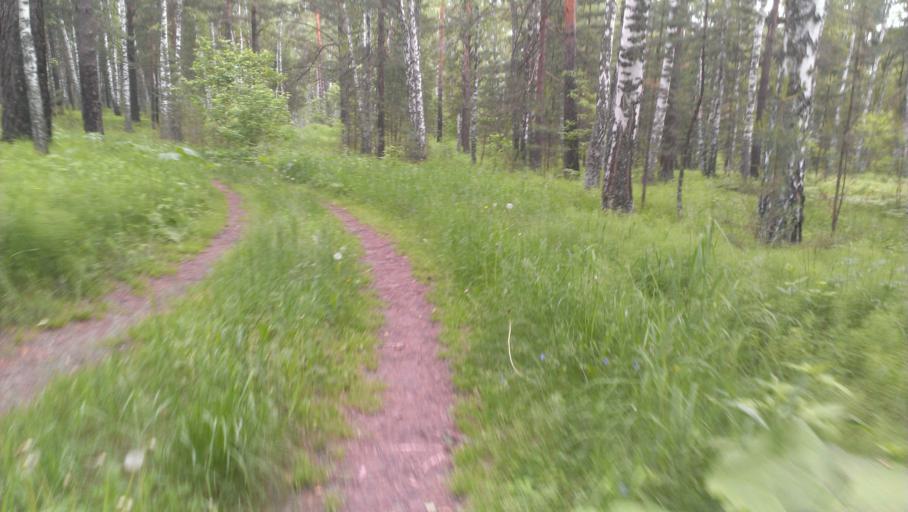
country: RU
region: Altai Krai
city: Sannikovo
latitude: 53.3424
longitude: 84.0459
